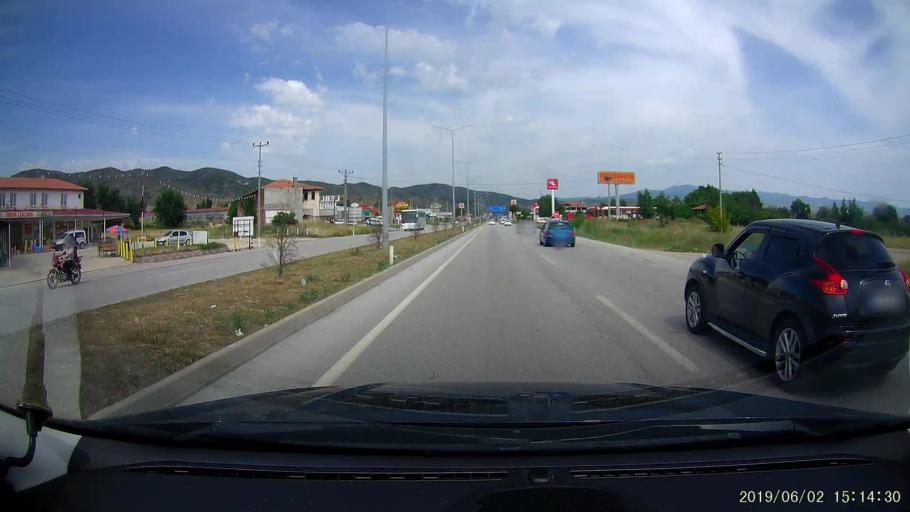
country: TR
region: Corum
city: Osmancik
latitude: 40.9706
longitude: 34.8367
